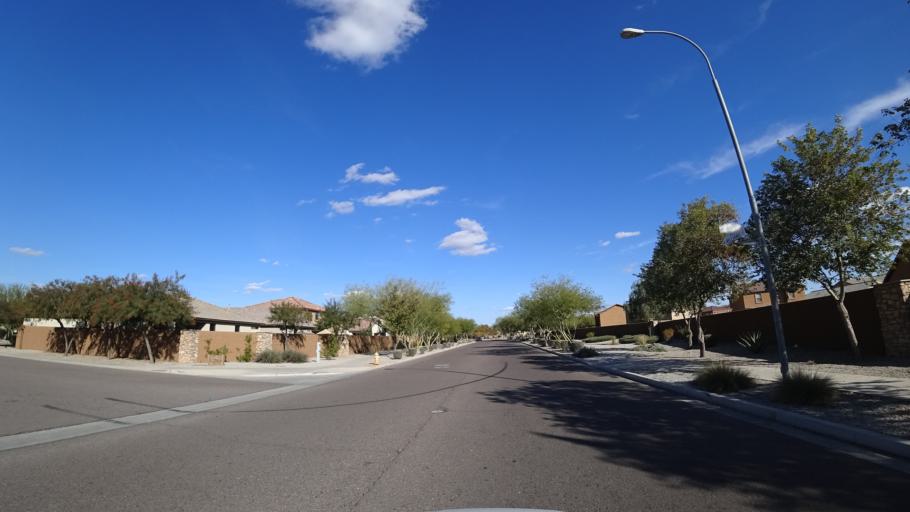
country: US
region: Arizona
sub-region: Maricopa County
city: Tolleson
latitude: 33.4199
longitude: -112.2488
